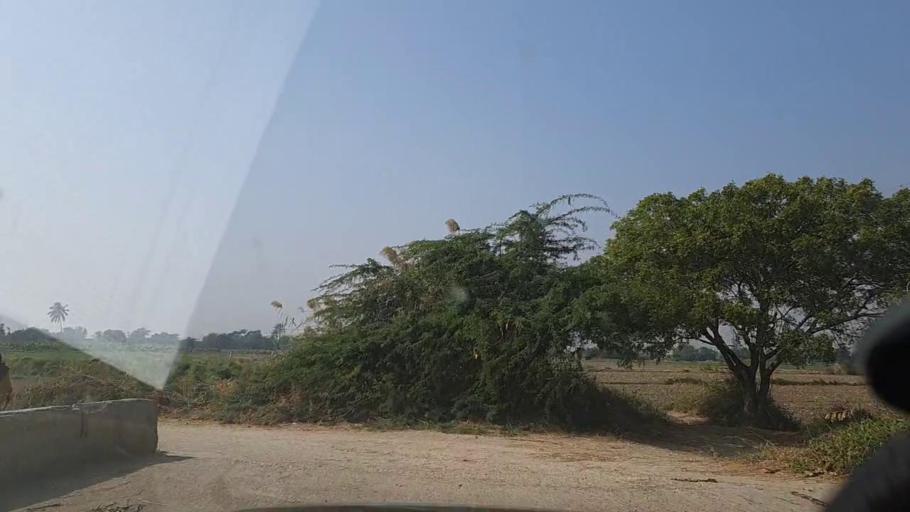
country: PK
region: Sindh
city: Thatta
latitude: 24.6538
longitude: 67.9106
